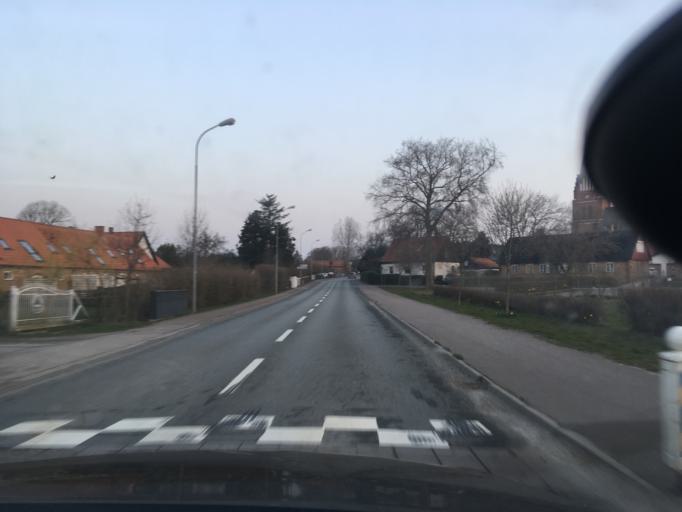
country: SE
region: Skane
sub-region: Ystads Kommun
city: Kopingebro
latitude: 55.4544
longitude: 14.0195
